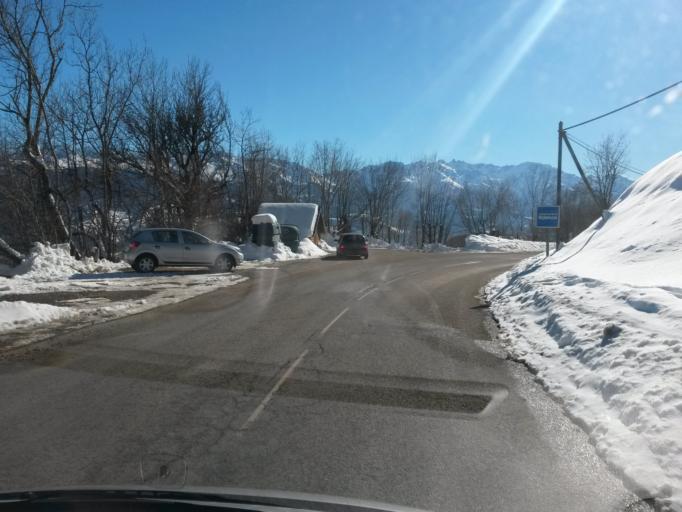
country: FR
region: Rhone-Alpes
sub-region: Departement de l'Isere
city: La Terrasse
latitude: 45.3426
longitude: 5.9051
